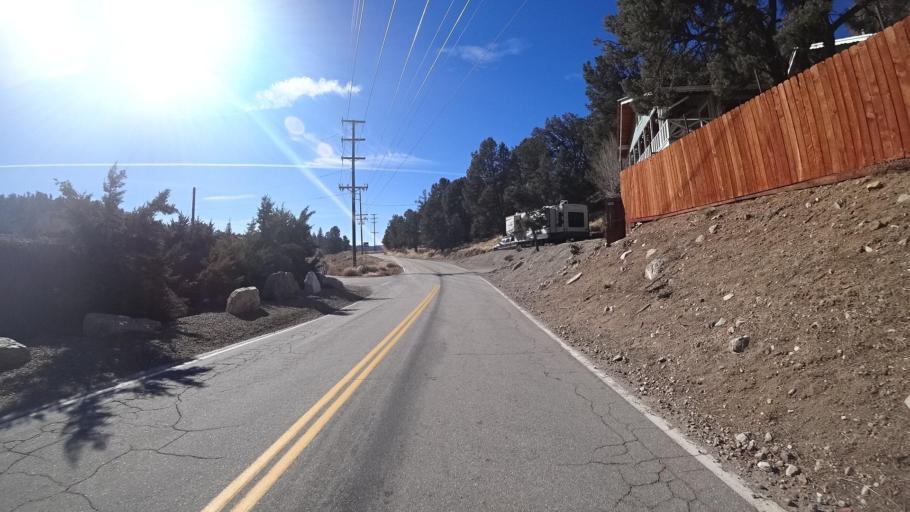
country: US
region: California
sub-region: Kern County
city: Frazier Park
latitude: 34.8175
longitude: -119.0048
